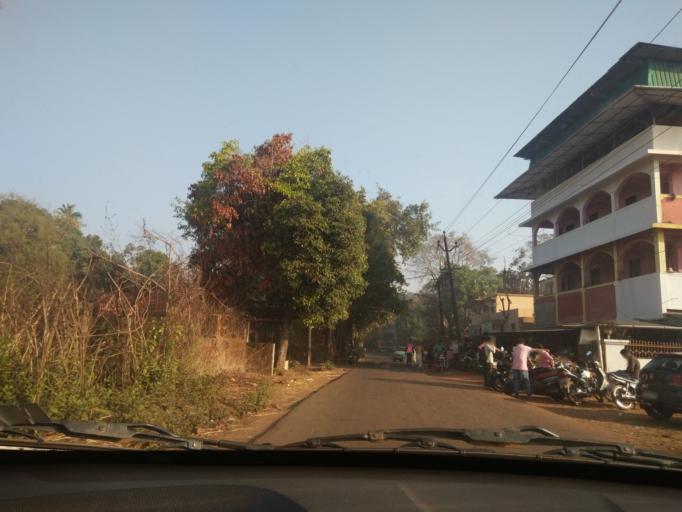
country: IN
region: Goa
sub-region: South Goa
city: Davorlim
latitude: 15.2776
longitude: 74.0058
